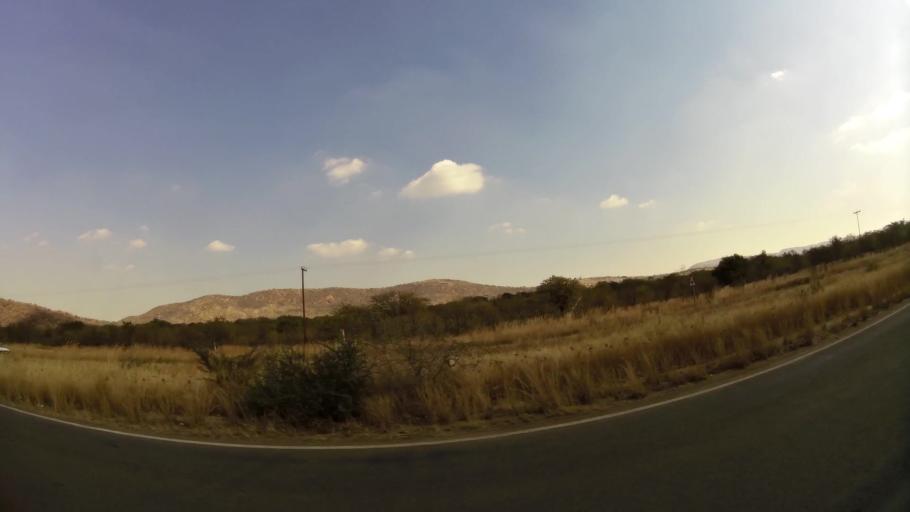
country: ZA
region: North-West
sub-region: Bojanala Platinum District Municipality
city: Rustenburg
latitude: -25.5336
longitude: 27.1182
